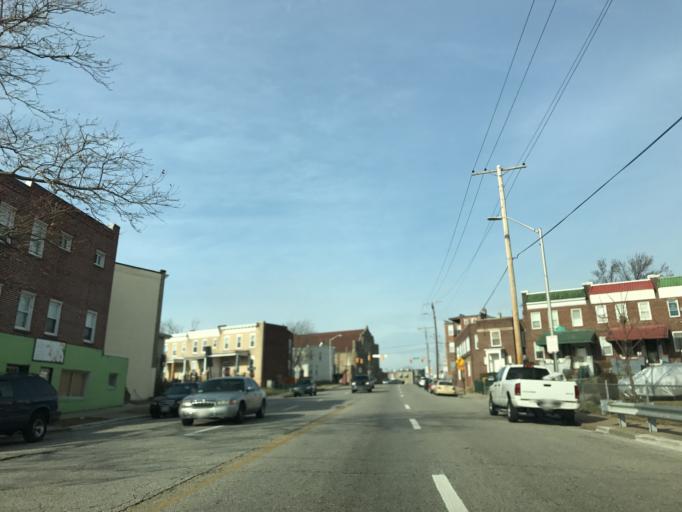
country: US
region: Maryland
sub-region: City of Baltimore
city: Baltimore
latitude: 39.3242
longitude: -76.5885
